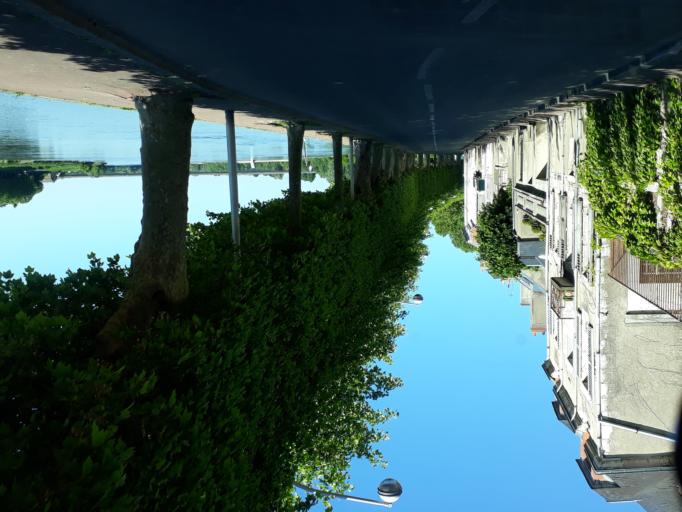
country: FR
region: Centre
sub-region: Departement du Loiret
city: Gien
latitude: 47.6830
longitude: 2.6337
